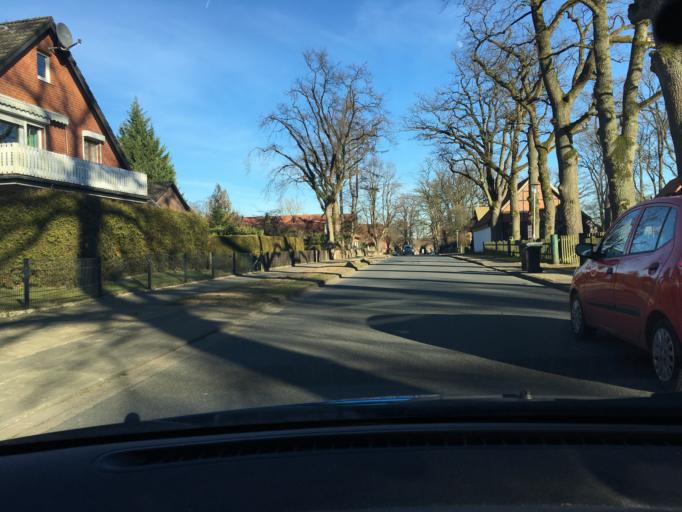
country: DE
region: Lower Saxony
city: Melbeck
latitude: 53.1781
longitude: 10.3992
